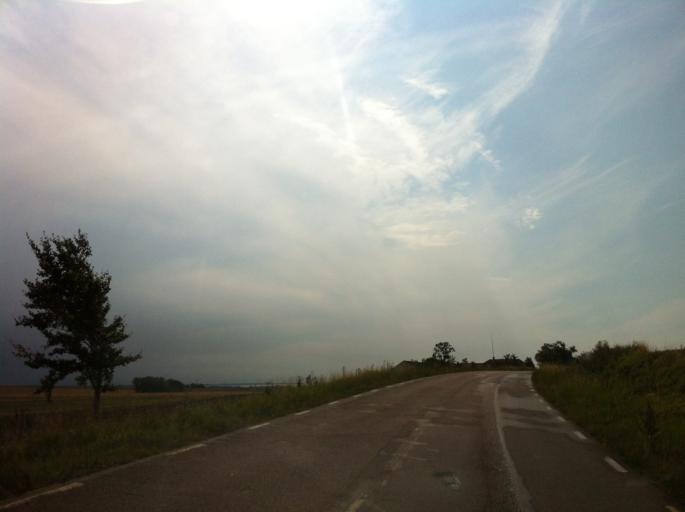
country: SE
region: Skane
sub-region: Helsingborg
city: Glumslov
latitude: 55.9283
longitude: 12.8742
